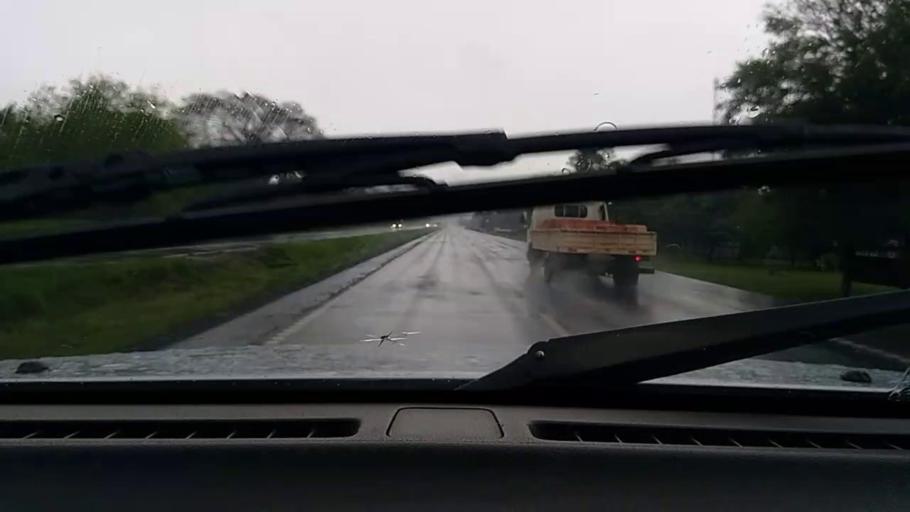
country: PY
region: Caaguazu
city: Repatriacion
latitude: -25.4580
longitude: -55.9188
